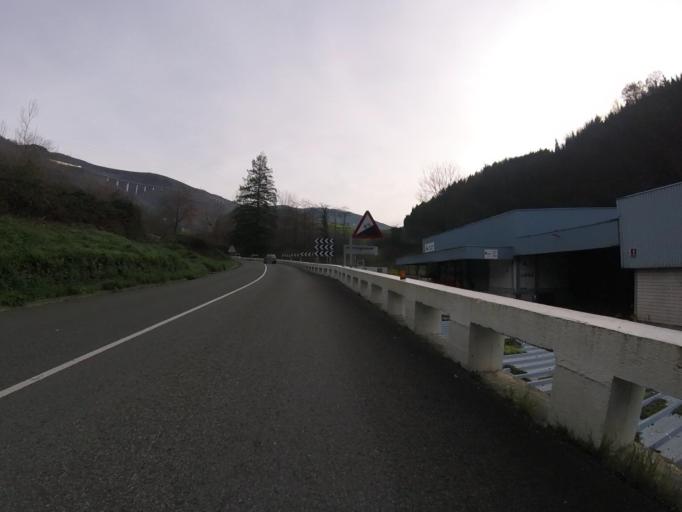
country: ES
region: Basque Country
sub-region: Provincia de Guipuzcoa
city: Elduayen
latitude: 43.1426
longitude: -2.0124
